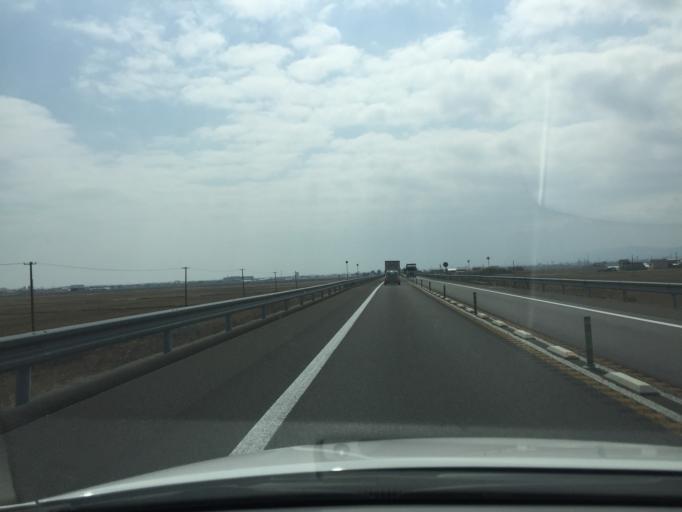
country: JP
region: Miyagi
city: Watari
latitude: 38.0625
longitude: 140.8935
